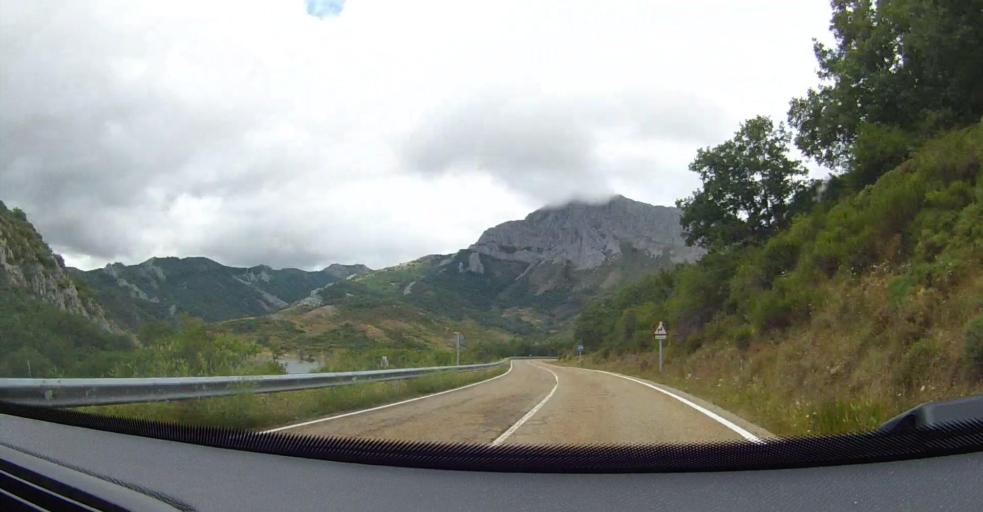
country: ES
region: Castille and Leon
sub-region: Provincia de Leon
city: Puebla de Lillo
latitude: 42.9731
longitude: -5.2587
